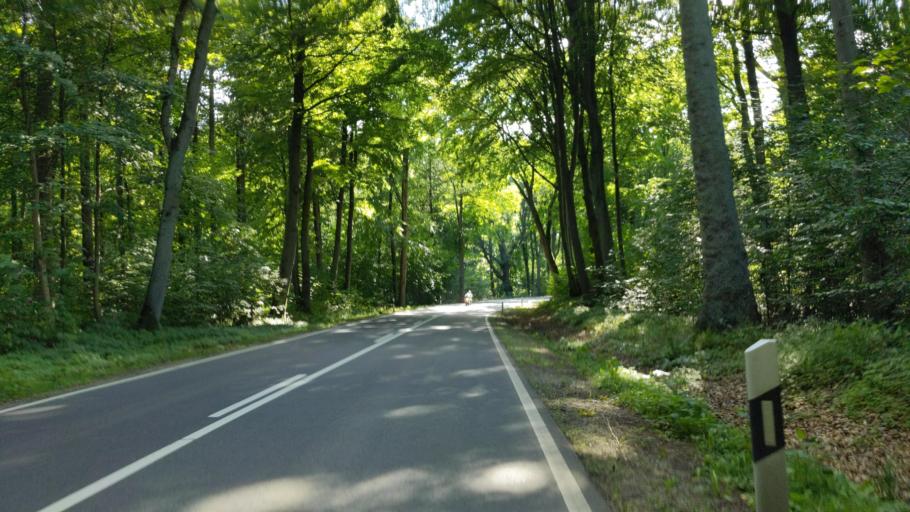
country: DE
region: Schleswig-Holstein
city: Kasseedorf
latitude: 54.1505
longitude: 10.7117
